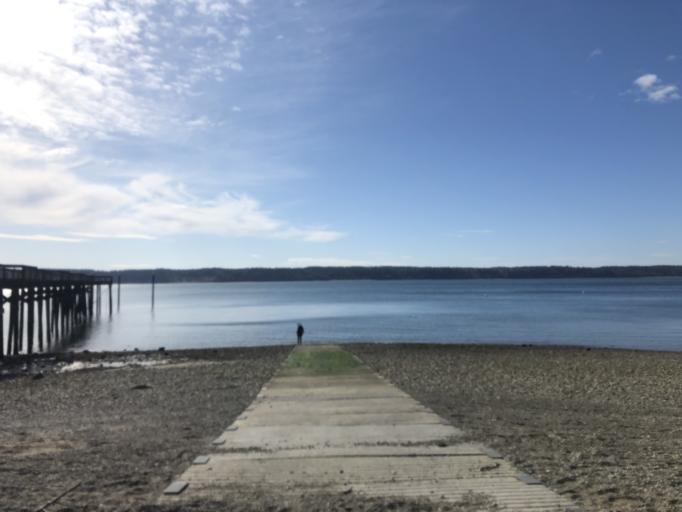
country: US
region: Washington
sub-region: Pierce County
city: Longbranch
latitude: 47.2250
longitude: -122.8097
